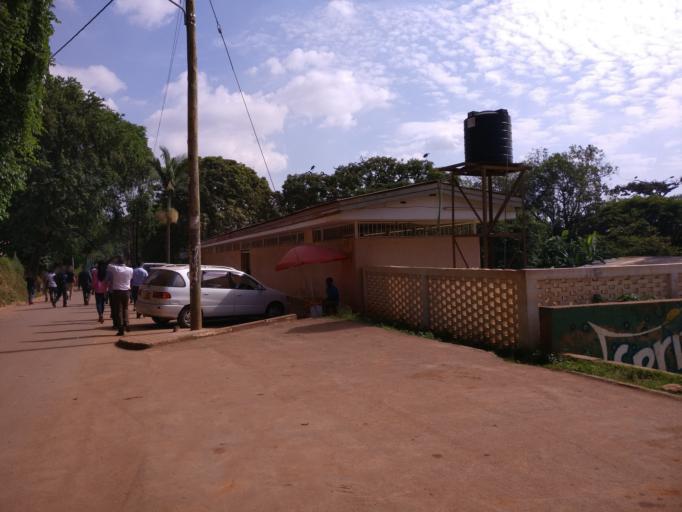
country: UG
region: Central Region
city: Kampala Central Division
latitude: 0.3347
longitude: 32.5692
